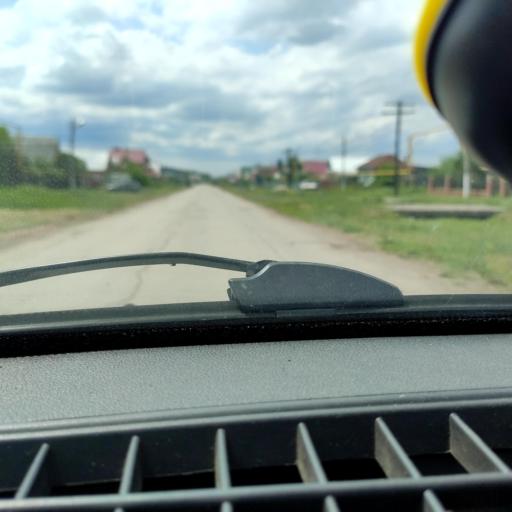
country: RU
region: Samara
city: Povolzhskiy
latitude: 53.6392
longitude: 49.6816
